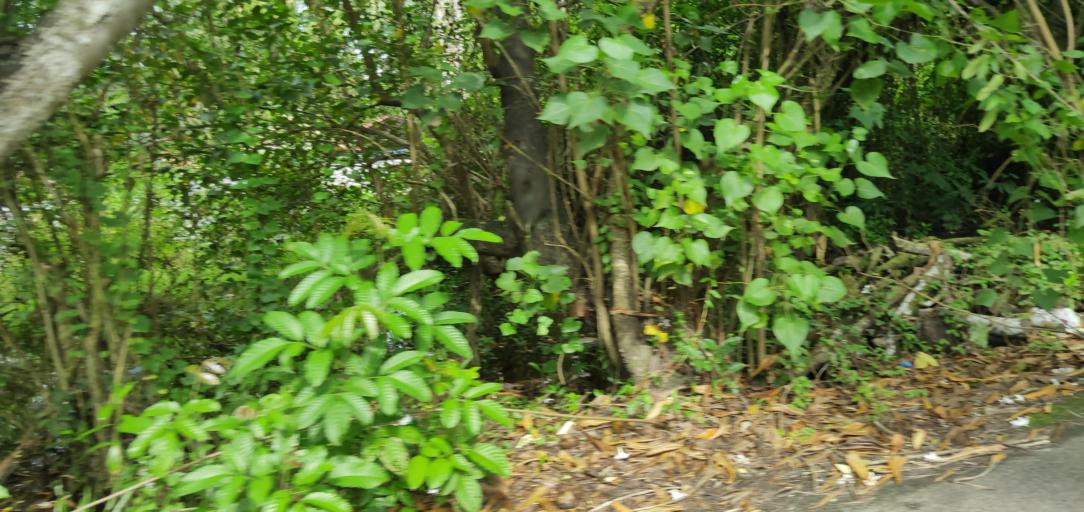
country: IN
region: Kerala
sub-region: Alappuzha
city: Kayankulam
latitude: 9.2296
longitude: 76.4578
